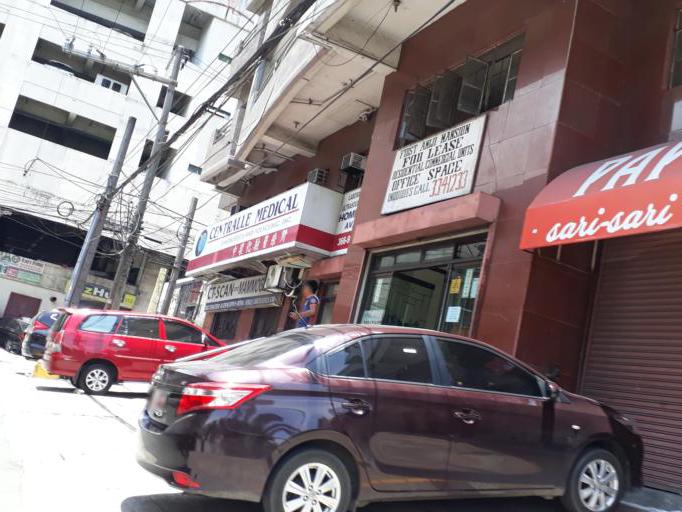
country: PH
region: Calabarzon
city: Del Monte
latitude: 14.6460
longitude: 120.9851
